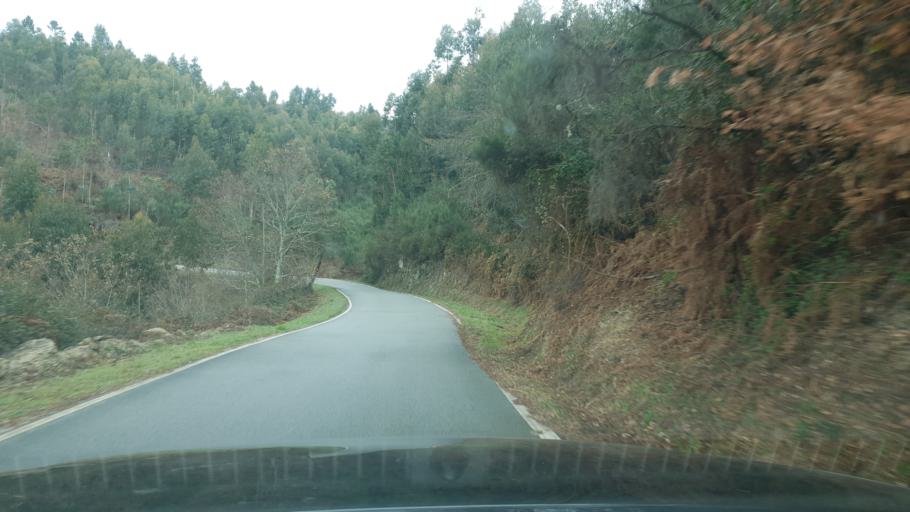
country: PT
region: Viseu
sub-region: Castro Daire
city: Castro Daire
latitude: 40.8857
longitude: -8.0139
